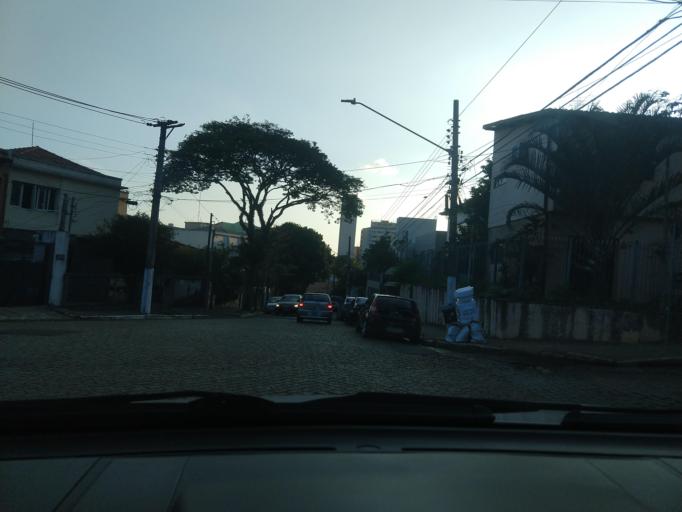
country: BR
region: Sao Paulo
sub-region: Sao Paulo
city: Sao Paulo
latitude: -23.5894
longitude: -46.6454
